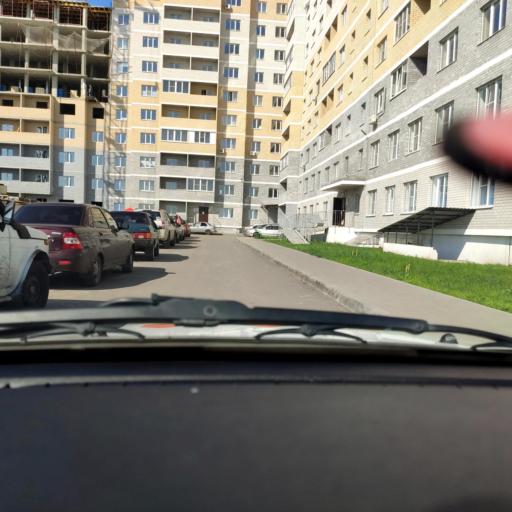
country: RU
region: Voronezj
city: Novaya Usman'
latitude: 51.6123
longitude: 39.3675
